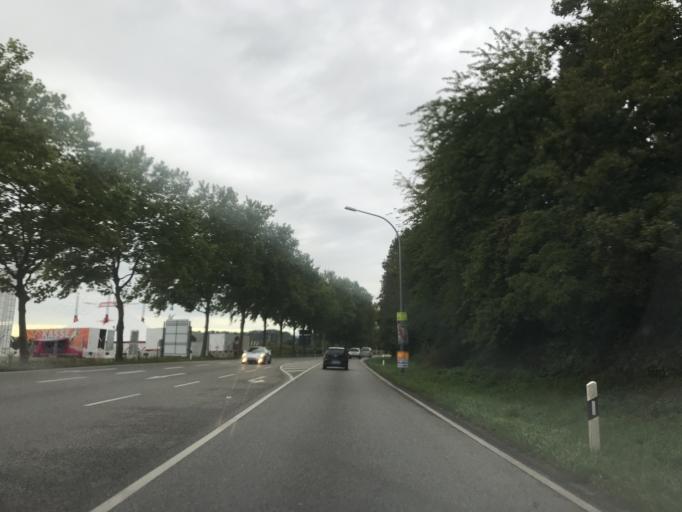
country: CH
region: Aargau
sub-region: Bezirk Rheinfelden
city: Mumpf
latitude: 47.5552
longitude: 7.9296
